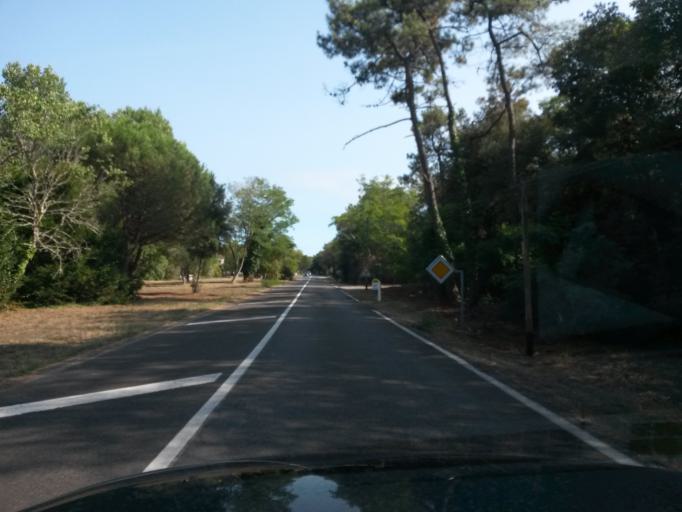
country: FR
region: Pays de la Loire
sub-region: Departement de la Vendee
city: Bretignolles-sur-Mer
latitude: 46.5851
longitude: -1.8280
